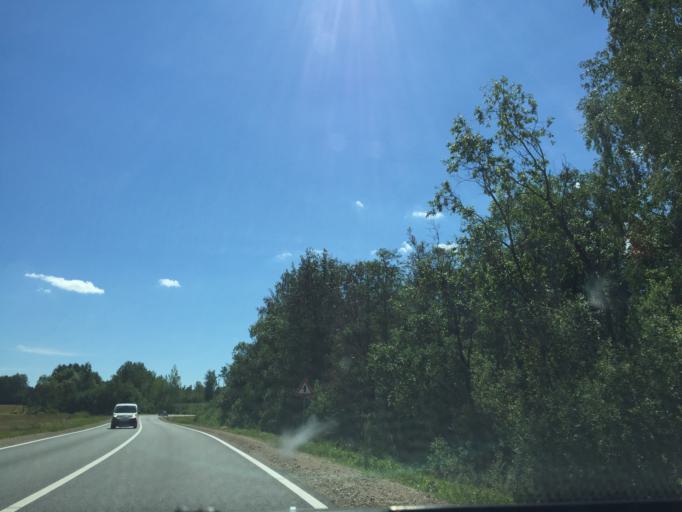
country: LV
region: Salas
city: Sala
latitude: 56.5497
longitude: 25.7979
